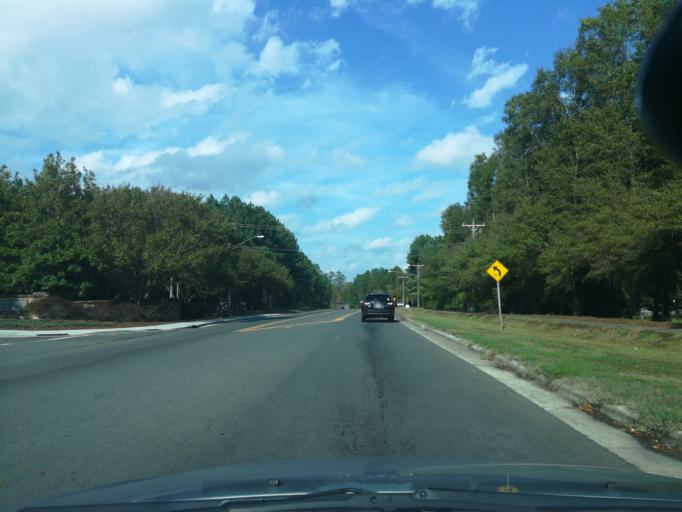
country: US
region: North Carolina
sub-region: Durham County
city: Durham
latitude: 36.0514
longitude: -78.9354
